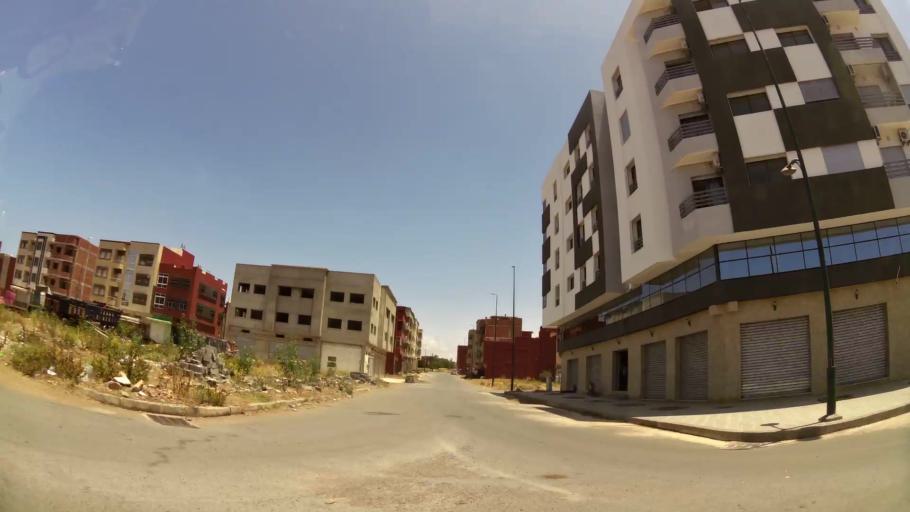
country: MA
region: Gharb-Chrarda-Beni Hssen
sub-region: Kenitra Province
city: Kenitra
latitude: 34.2675
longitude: -6.6266
